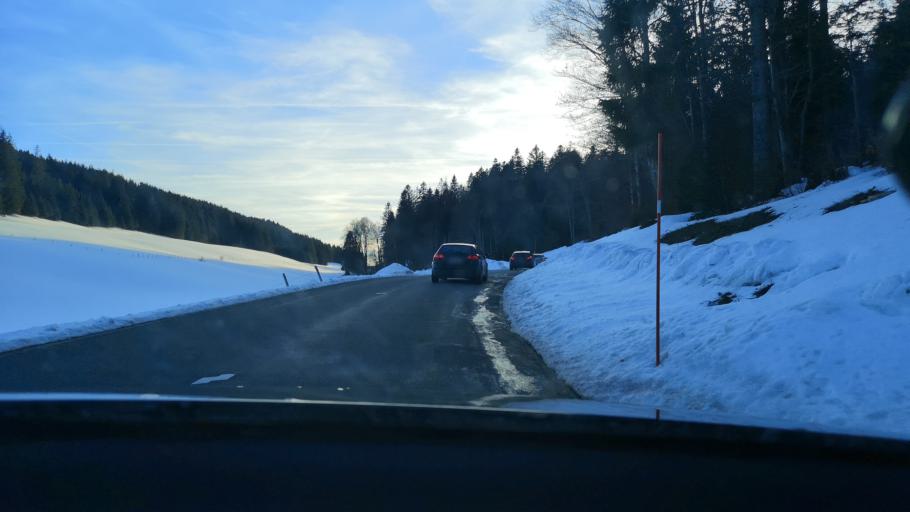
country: FR
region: Franche-Comte
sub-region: Departement du Doubs
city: Gilley
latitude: 46.9794
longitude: 6.4967
